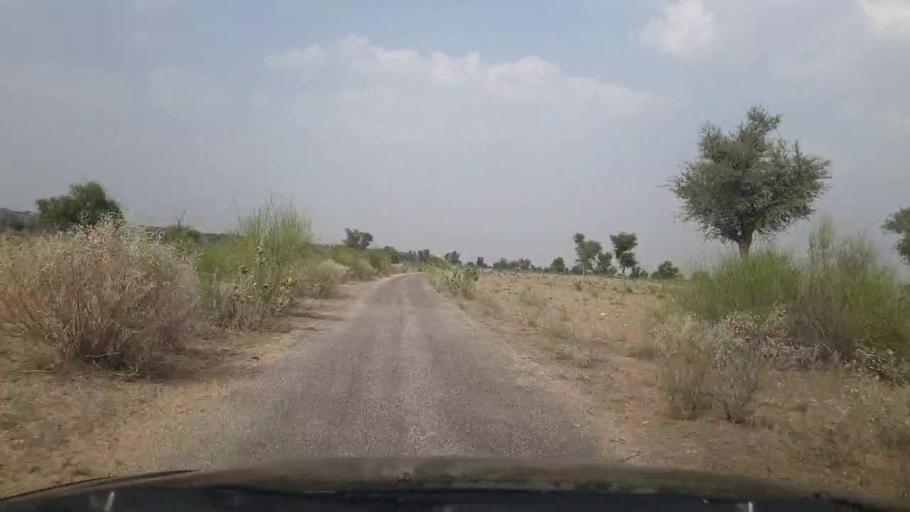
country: PK
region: Sindh
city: Islamkot
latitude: 24.9064
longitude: 70.5589
